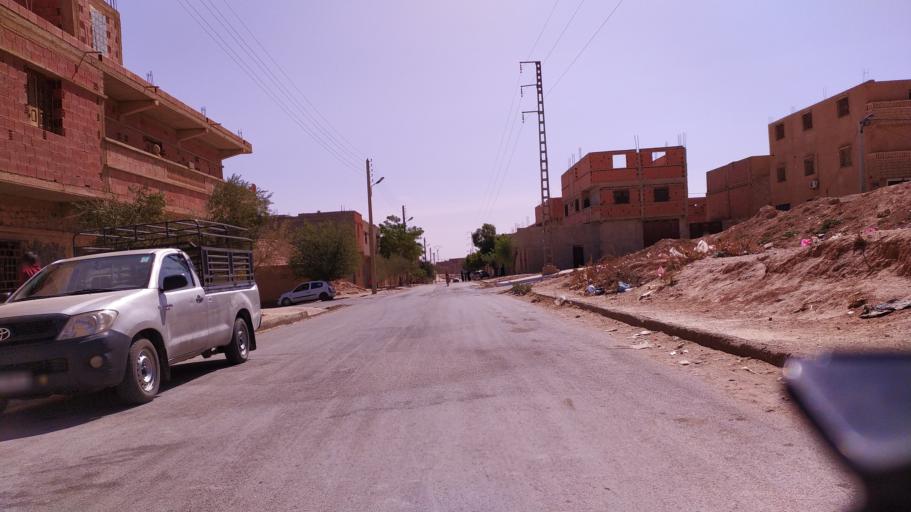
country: DZ
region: Tiaret
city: Frenda
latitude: 34.8920
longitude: 1.2428
